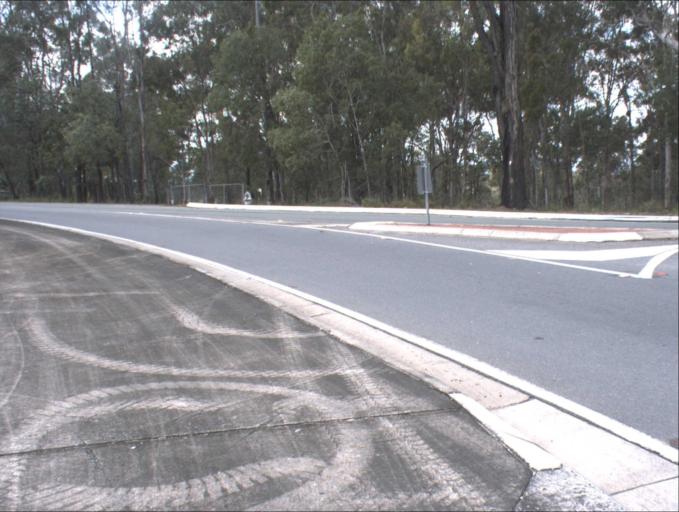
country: AU
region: Queensland
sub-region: Logan
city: North Maclean
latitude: -27.7384
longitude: 152.9829
